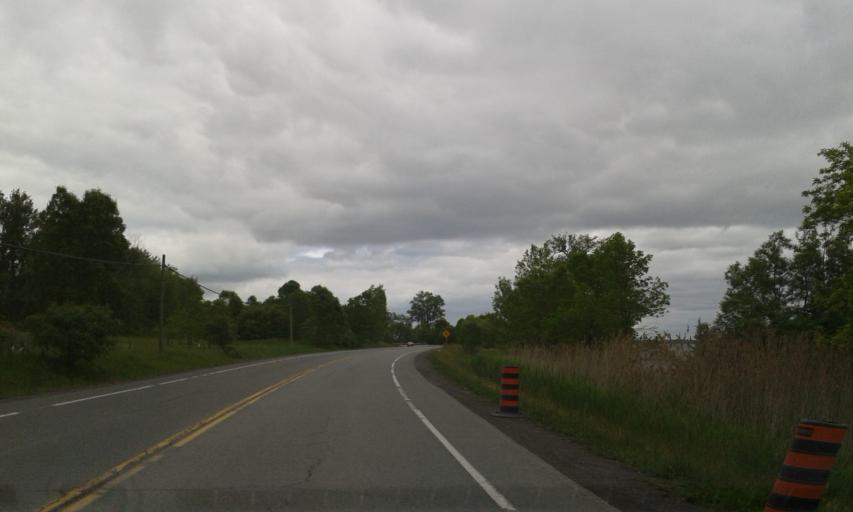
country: CA
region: Ontario
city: Skatepark
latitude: 44.1665
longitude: -76.7978
